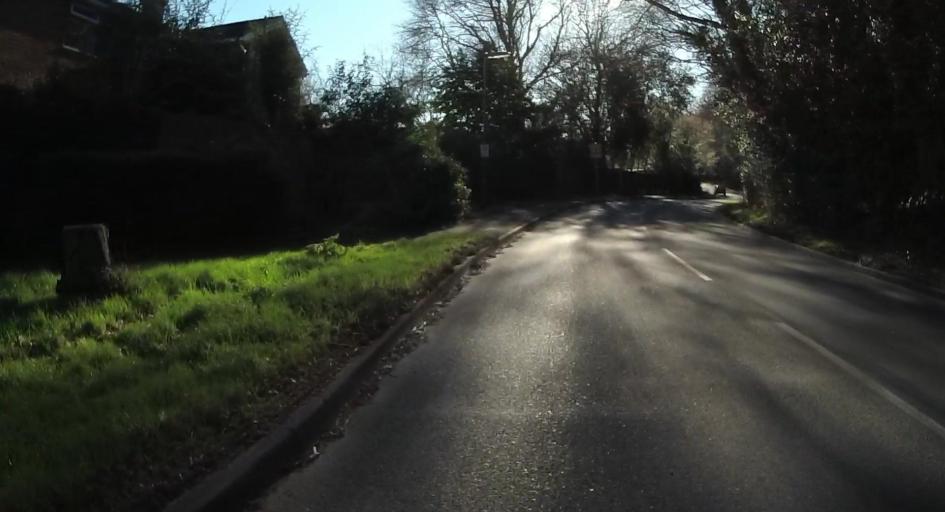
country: GB
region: England
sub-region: Surrey
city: Knaphill
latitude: 51.3223
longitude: -0.6193
